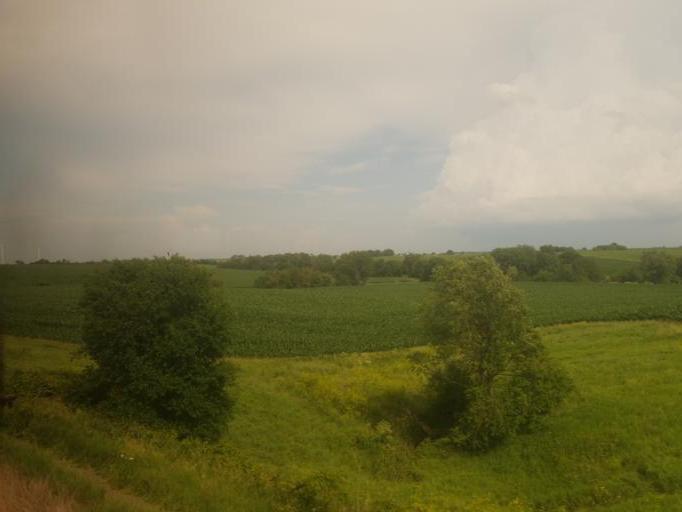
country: US
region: Illinois
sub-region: Henry County
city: Galva
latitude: 41.1450
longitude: -90.0913
